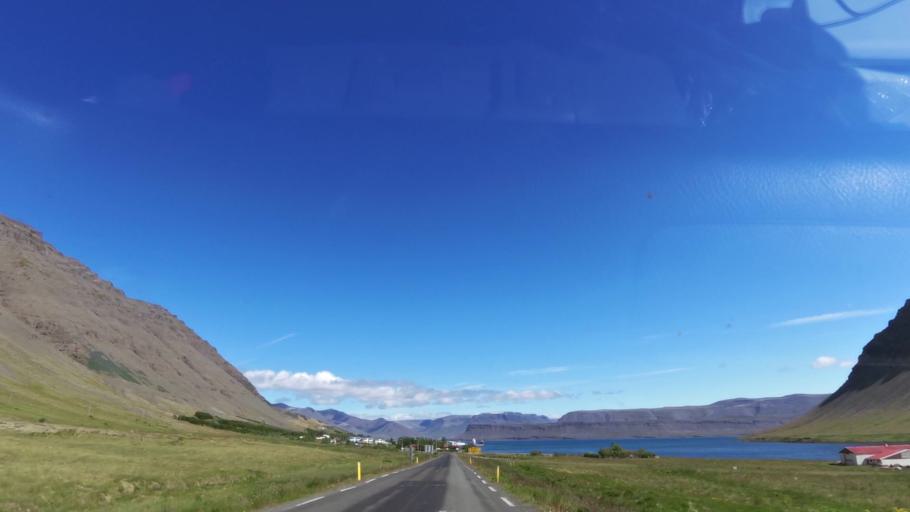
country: IS
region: Westfjords
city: Isafjoerdur
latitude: 65.6747
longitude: -23.6174
